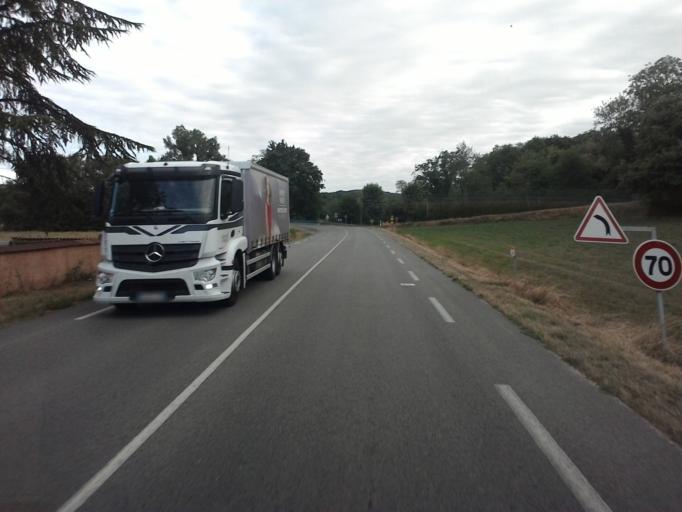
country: FR
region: Rhone-Alpes
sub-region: Departement de l'Ain
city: Saint-Martin-du-Mont
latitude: 46.0630
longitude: 5.3313
